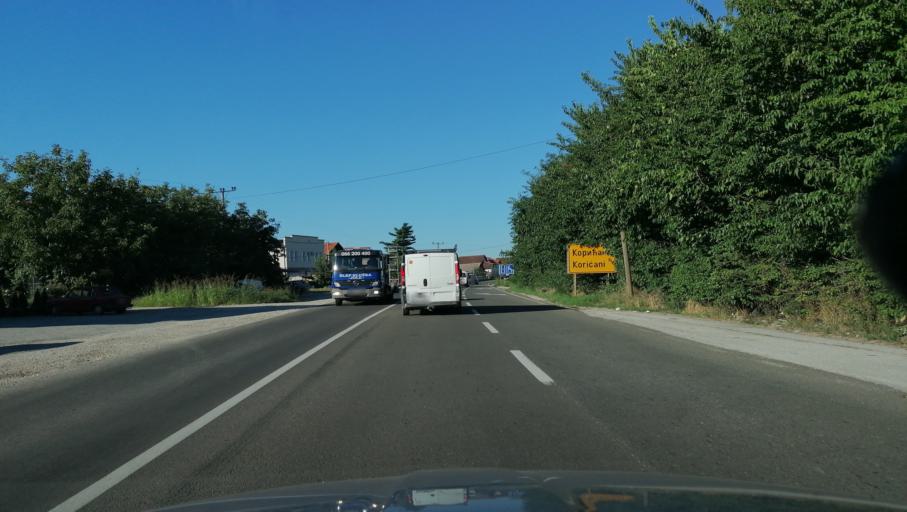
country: RS
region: Central Serbia
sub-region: Sumadijski Okrug
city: Kragujevac
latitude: 43.9805
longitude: 20.8296
